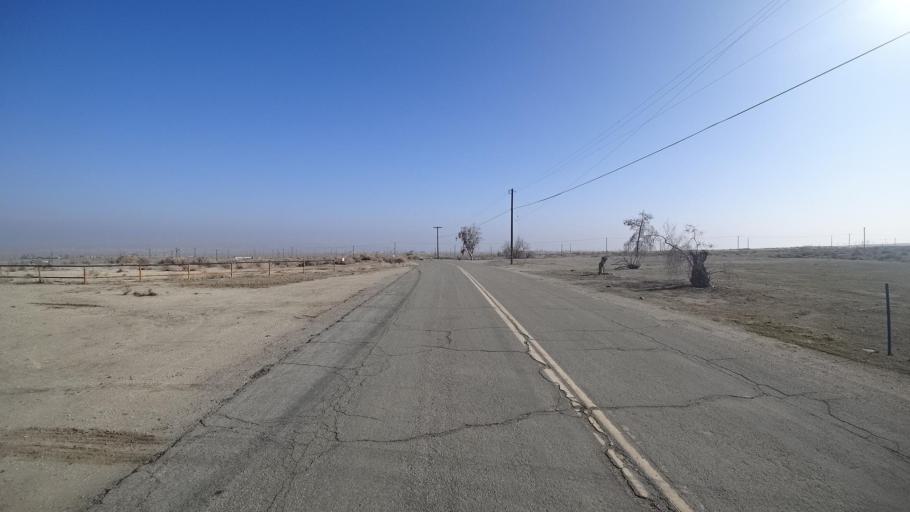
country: US
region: California
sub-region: Kern County
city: Taft Heights
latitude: 35.1765
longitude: -119.5385
